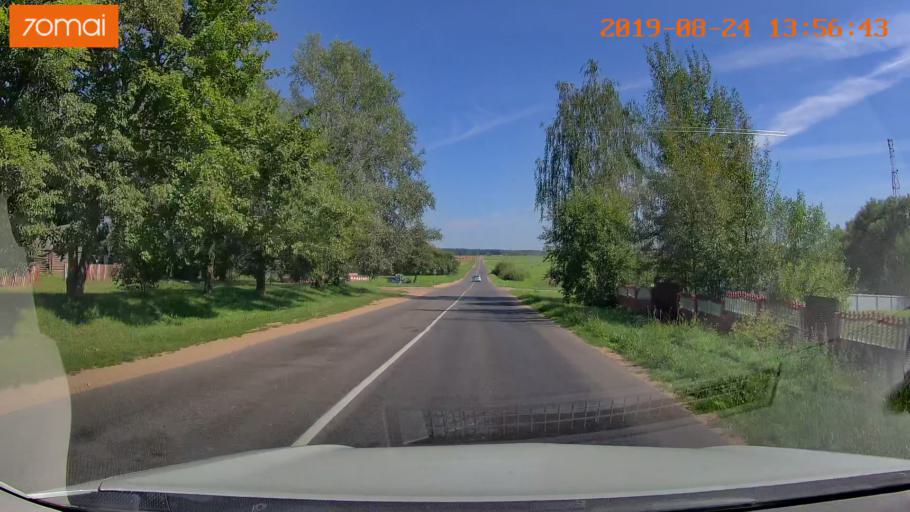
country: BY
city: Michanovichi
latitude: 53.6087
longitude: 27.6438
